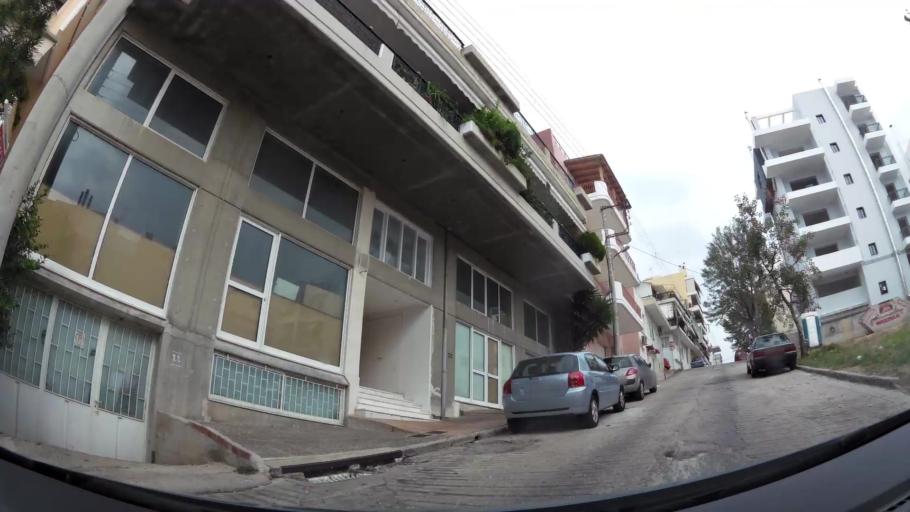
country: GR
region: Attica
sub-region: Nomarchia Athinas
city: Agios Dimitrios
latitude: 37.9233
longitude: 23.7336
